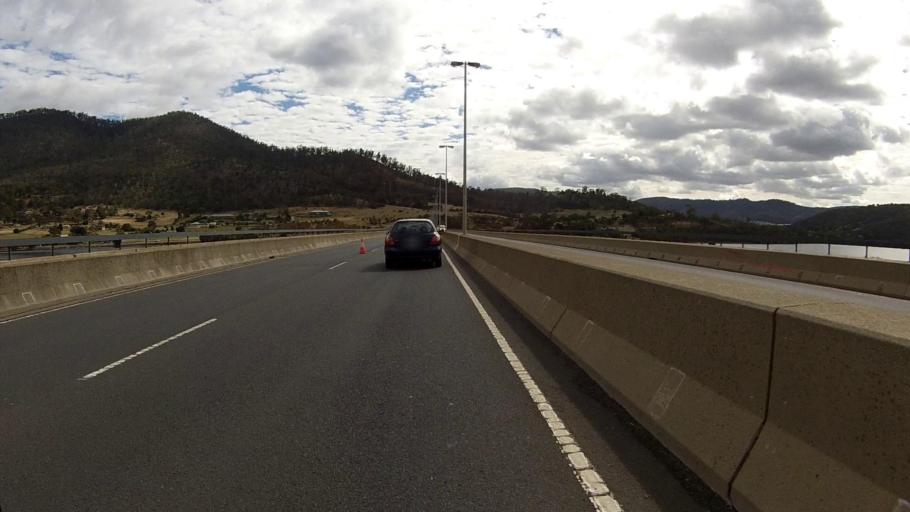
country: AU
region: Tasmania
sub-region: Glenorchy
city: Goodwood
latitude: -42.8178
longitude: 147.3069
